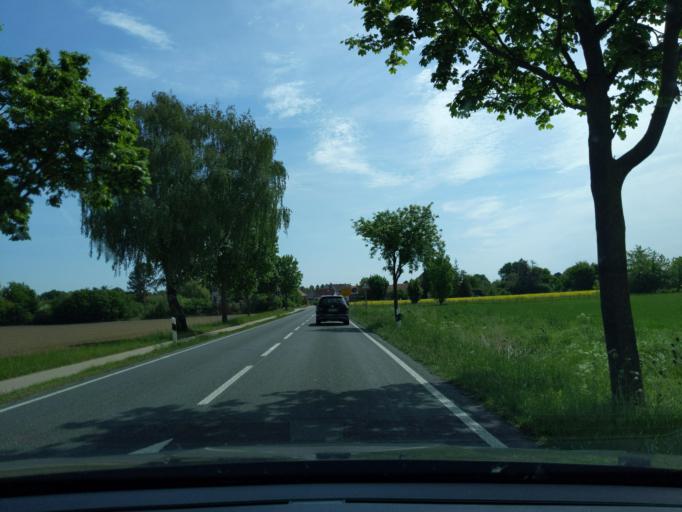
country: DE
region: Lower Saxony
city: Pattensen
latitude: 52.2143
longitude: 9.6949
